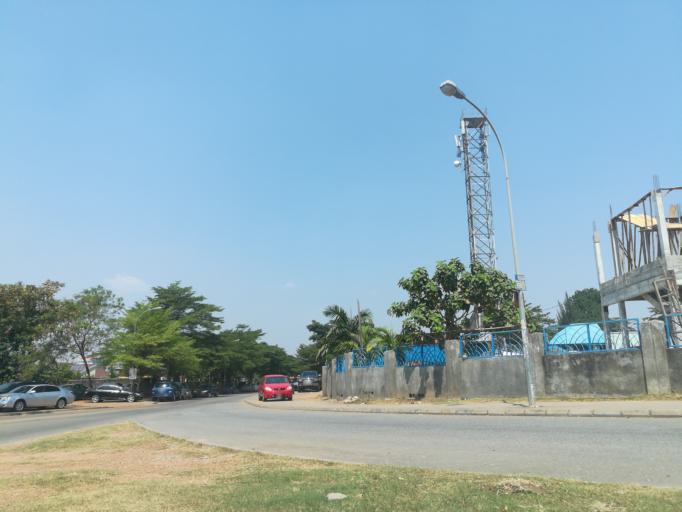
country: NG
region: Abuja Federal Capital Territory
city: Abuja
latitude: 9.0720
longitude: 7.4383
